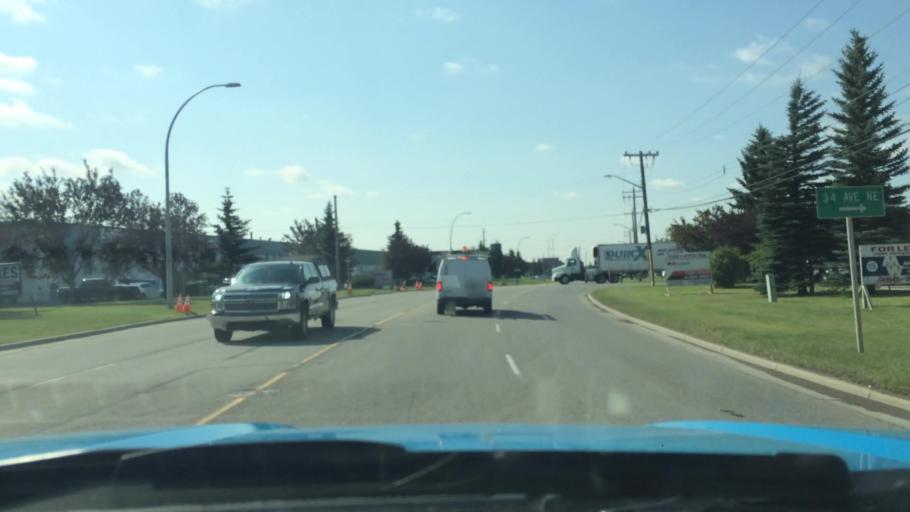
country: CA
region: Alberta
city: Calgary
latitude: 51.0843
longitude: -114.0298
